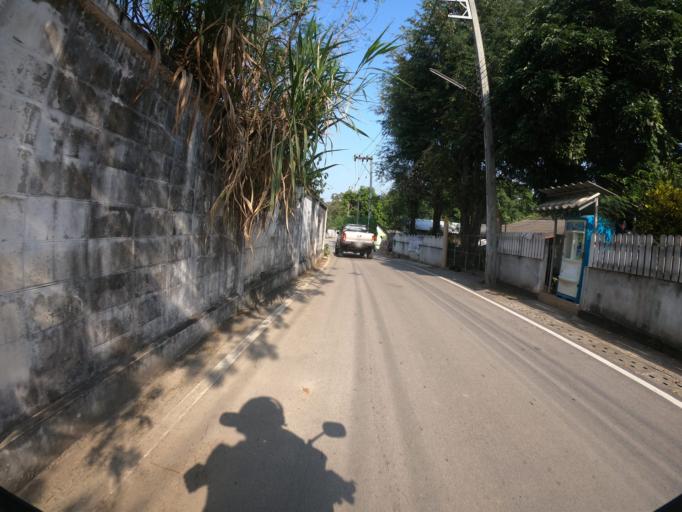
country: TH
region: Chiang Mai
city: Chiang Mai
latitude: 18.7526
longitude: 98.9386
